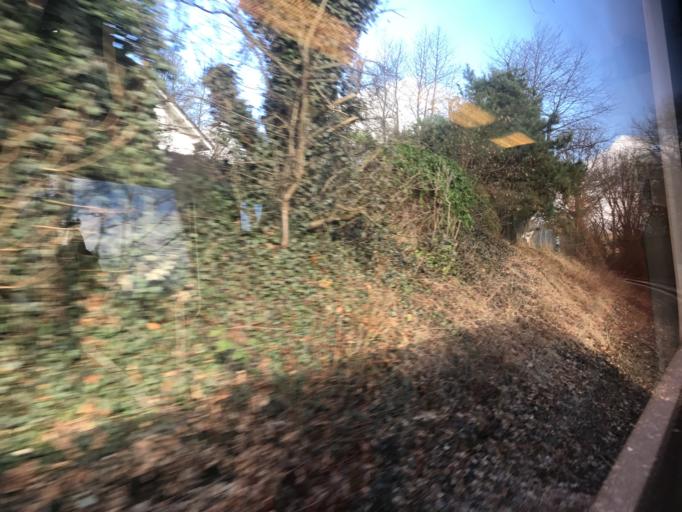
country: DE
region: Hesse
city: Kelkheim (Taunus)
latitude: 50.1495
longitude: 8.4481
